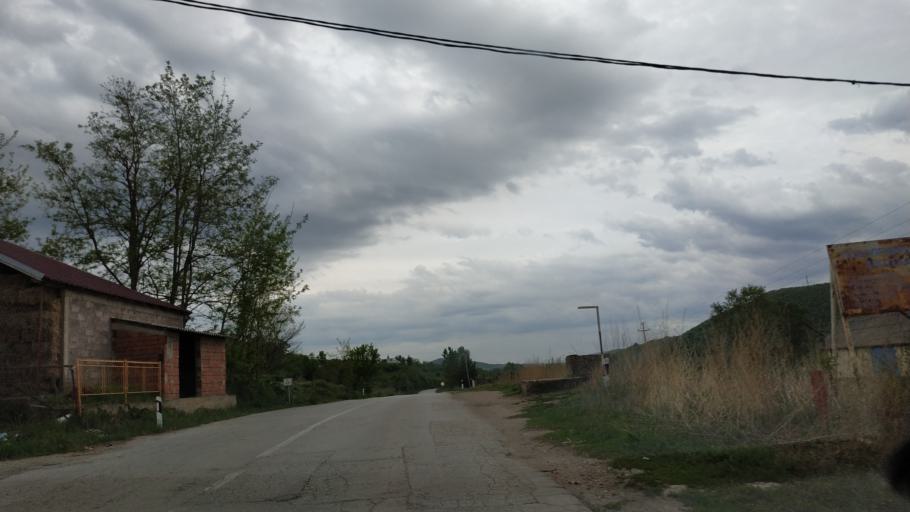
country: RS
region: Central Serbia
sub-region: Nisavski Okrug
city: Aleksinac
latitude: 43.5955
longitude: 21.6905
